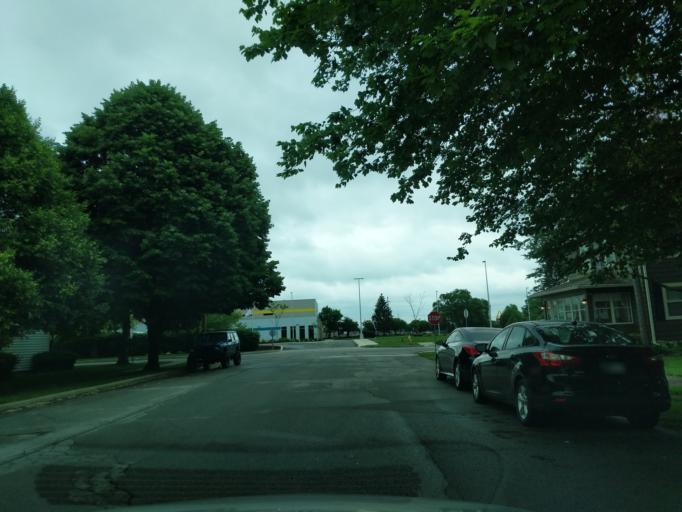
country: US
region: Indiana
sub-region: Hamilton County
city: Noblesville
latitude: 40.0465
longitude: -86.0041
